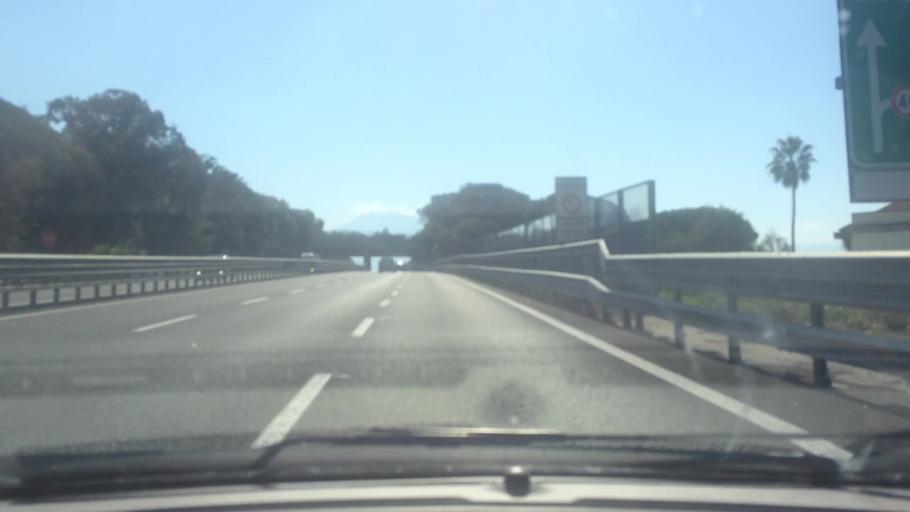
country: IT
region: Campania
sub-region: Provincia di Napoli
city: Ercolano
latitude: 40.7987
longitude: 14.3714
